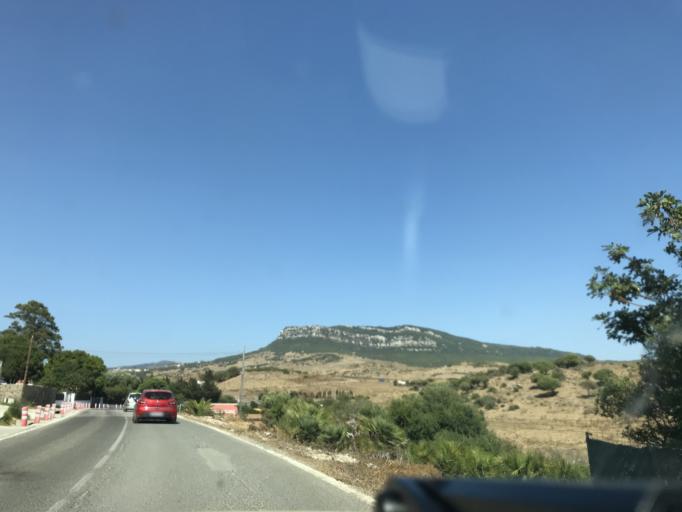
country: ES
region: Andalusia
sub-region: Provincia de Cadiz
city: Zahara de los Atunes
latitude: 36.0877
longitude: -5.7641
